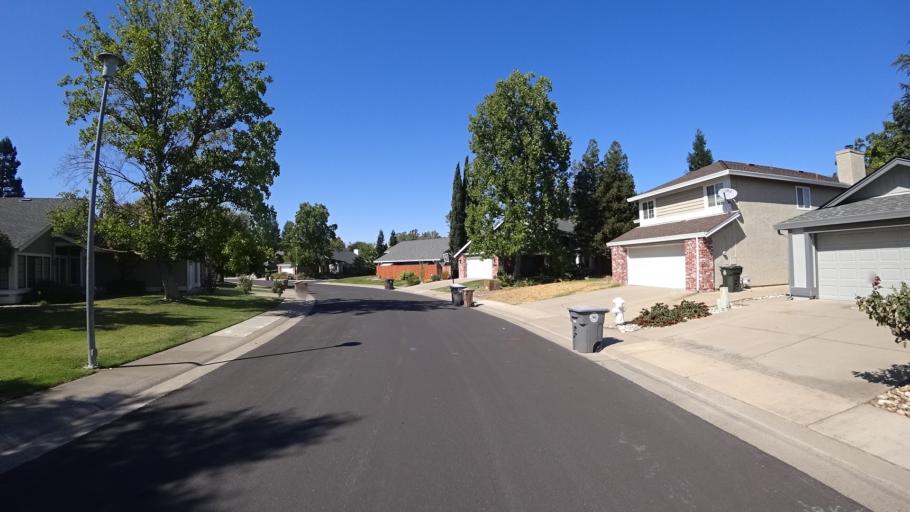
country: US
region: California
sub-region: Sacramento County
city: Laguna
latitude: 38.4268
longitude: -121.4332
